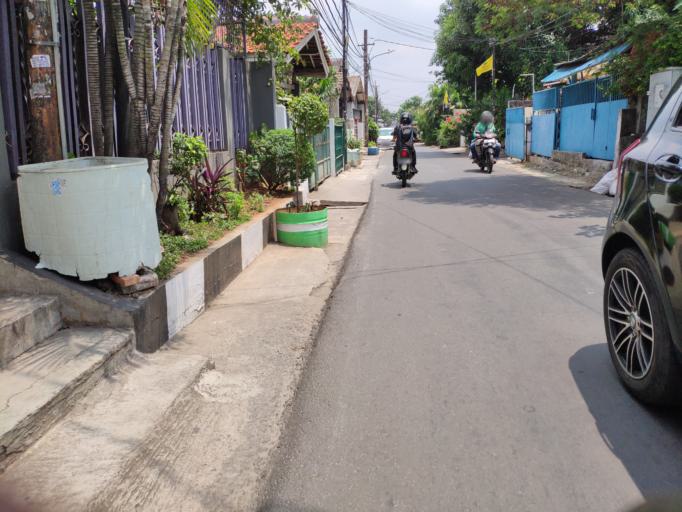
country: ID
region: Jakarta Raya
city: Jakarta
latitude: -6.2090
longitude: 106.8641
